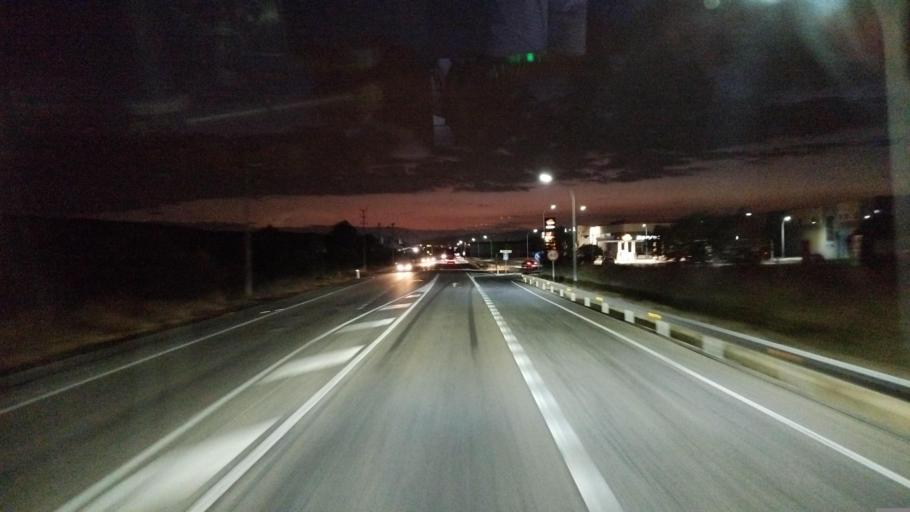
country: ES
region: Catalonia
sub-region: Provincia de Tarragona
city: Santa Oliva
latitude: 41.2352
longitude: 1.5677
